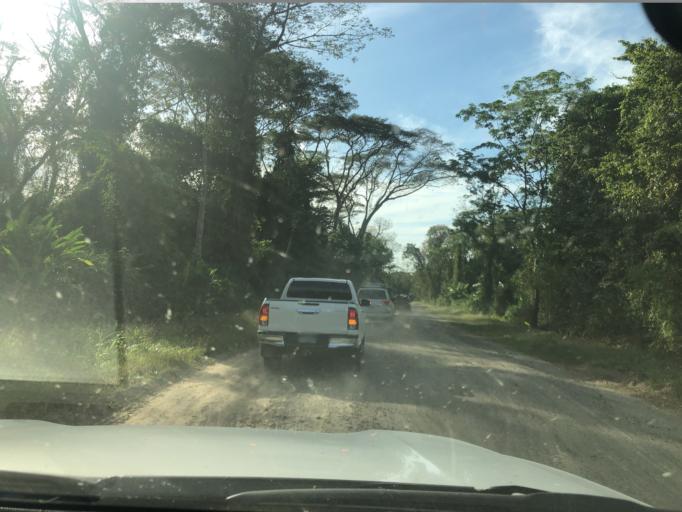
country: CR
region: Alajuela
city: San Jose
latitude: 11.1032
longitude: -85.2732
